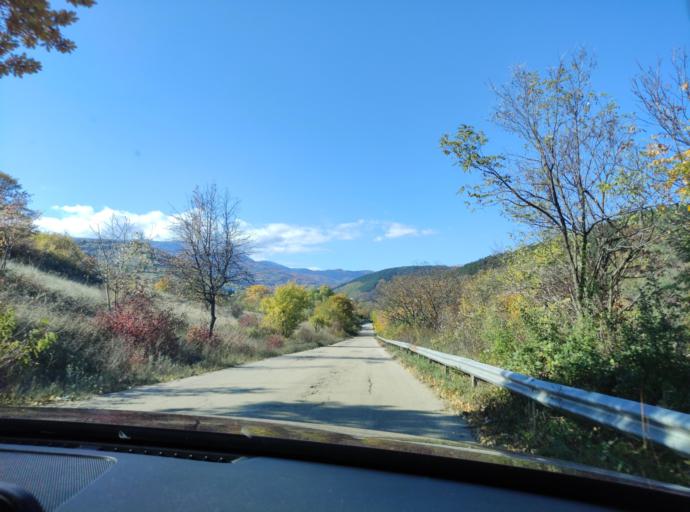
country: BG
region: Montana
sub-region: Obshtina Chiprovtsi
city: Chiprovtsi
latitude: 43.3798
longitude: 22.9100
